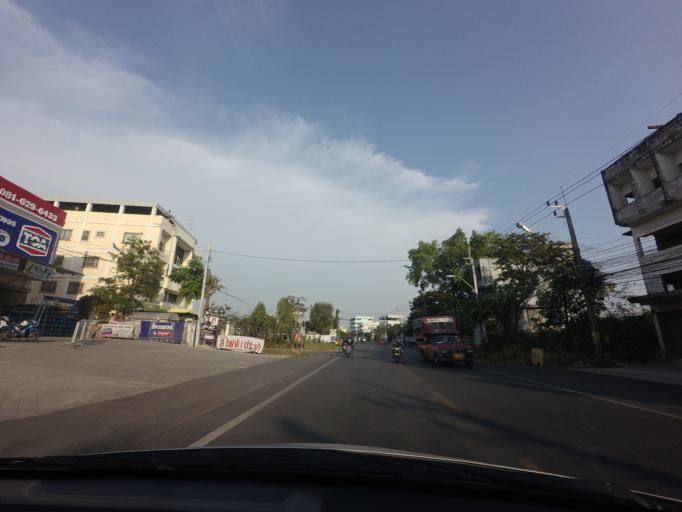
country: TH
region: Bangkok
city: Saphan Sung
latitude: 13.7411
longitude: 100.6837
